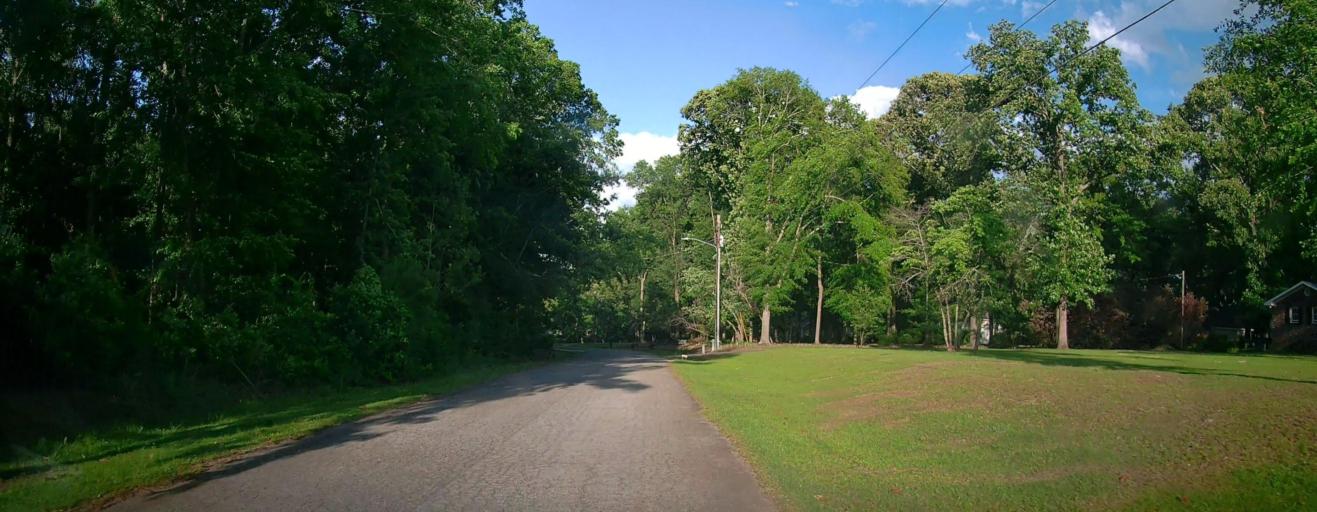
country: US
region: Georgia
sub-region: Peach County
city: Byron
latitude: 32.6403
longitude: -83.7551
